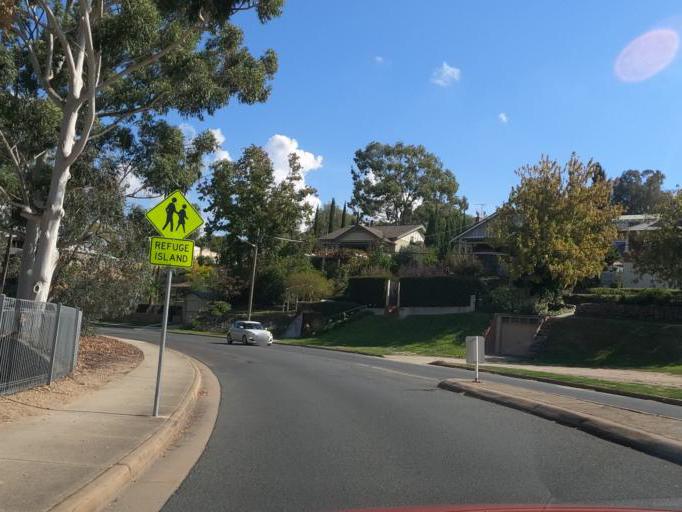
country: AU
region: New South Wales
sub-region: Albury Municipality
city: South Albury
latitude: -36.0802
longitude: 146.9090
